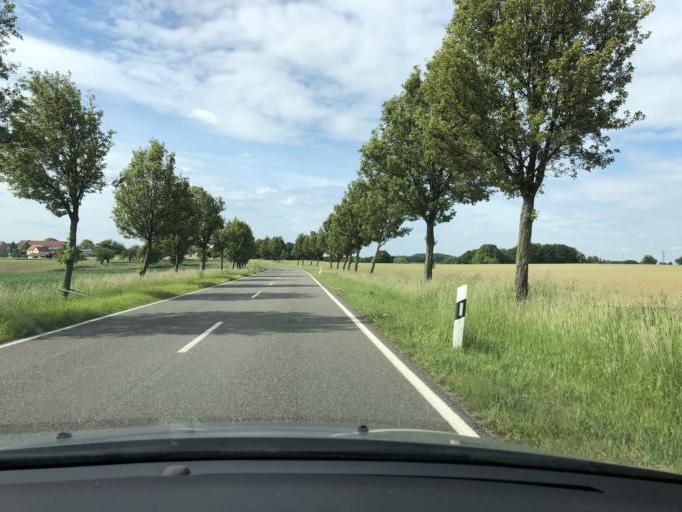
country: DE
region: Saxony
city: Nerchau
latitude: 51.2241
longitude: 12.8015
